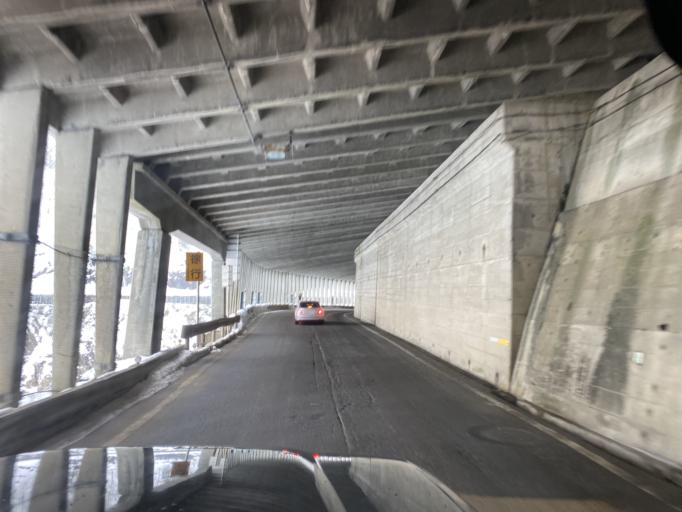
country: JP
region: Gifu
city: Takayama
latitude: 36.1284
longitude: 136.9097
